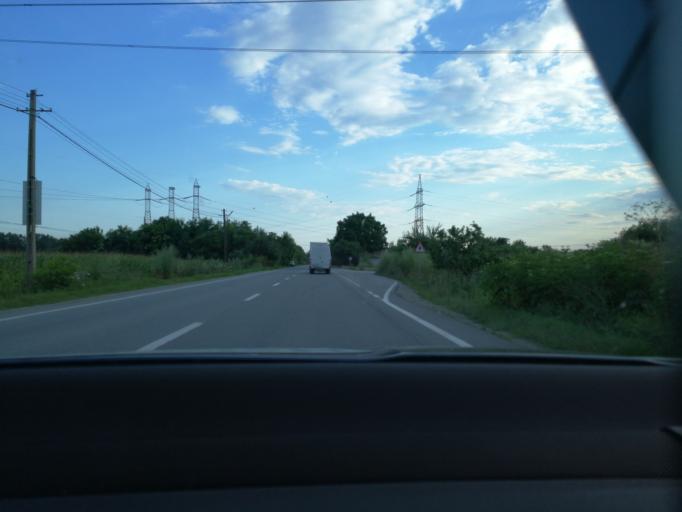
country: RO
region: Prahova
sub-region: Comuna Targsoru Vechi
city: Targsoru Vechi
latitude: 44.8605
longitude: 25.9265
